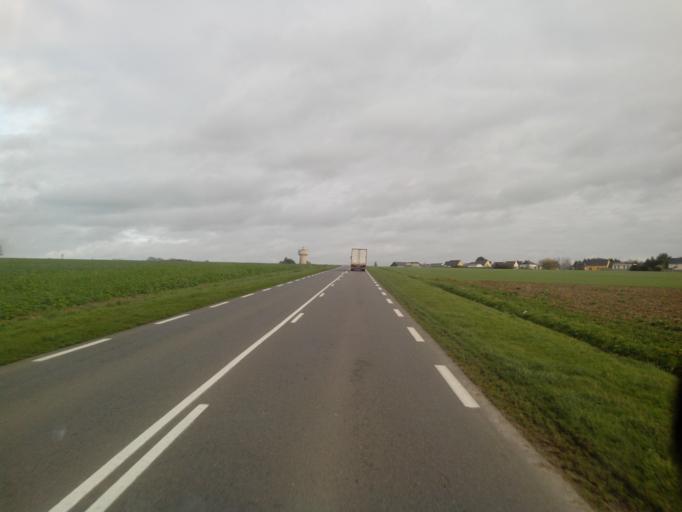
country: FR
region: Brittany
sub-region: Departement d'Ille-et-Vilaine
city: Gael
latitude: 48.1374
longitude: -2.2260
